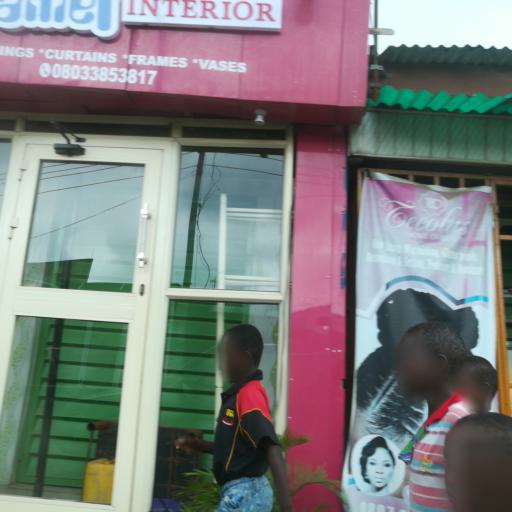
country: NG
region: Lagos
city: Agege
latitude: 6.6000
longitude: 3.3010
